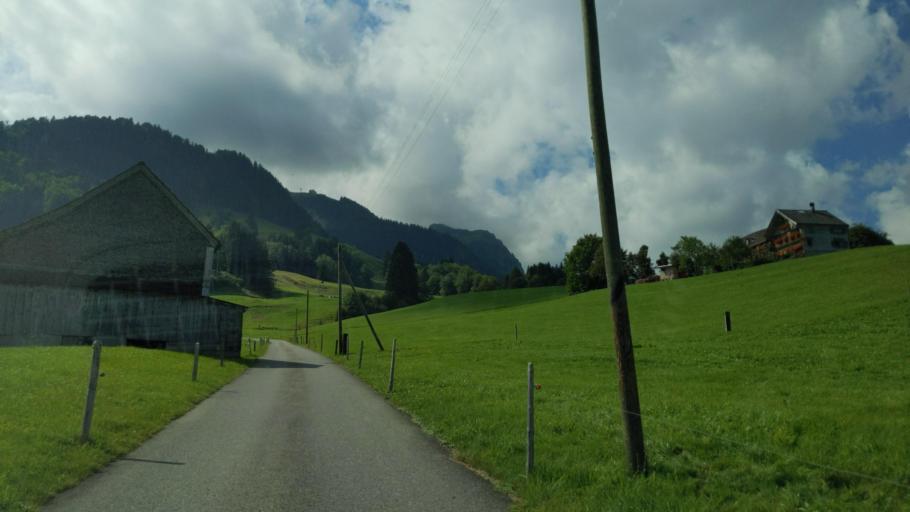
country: CH
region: Appenzell Innerrhoden
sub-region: Appenzell Inner Rhodes
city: Appenzell
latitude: 47.3020
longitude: 9.4285
